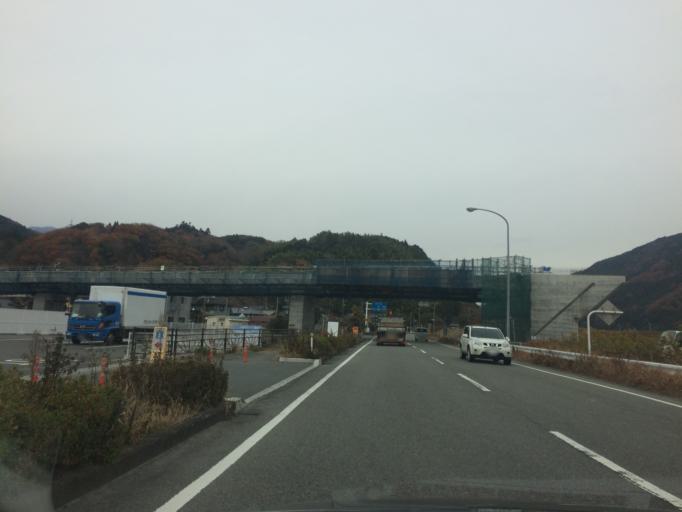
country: JP
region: Shizuoka
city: Fujinomiya
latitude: 35.2498
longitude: 138.4804
